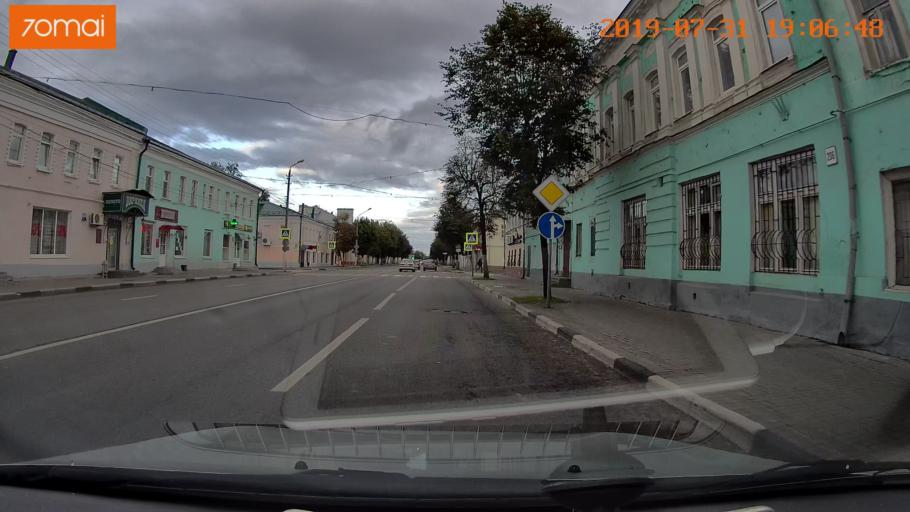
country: RU
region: Moskovskaya
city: Kolomna
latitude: 55.1006
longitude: 38.7563
